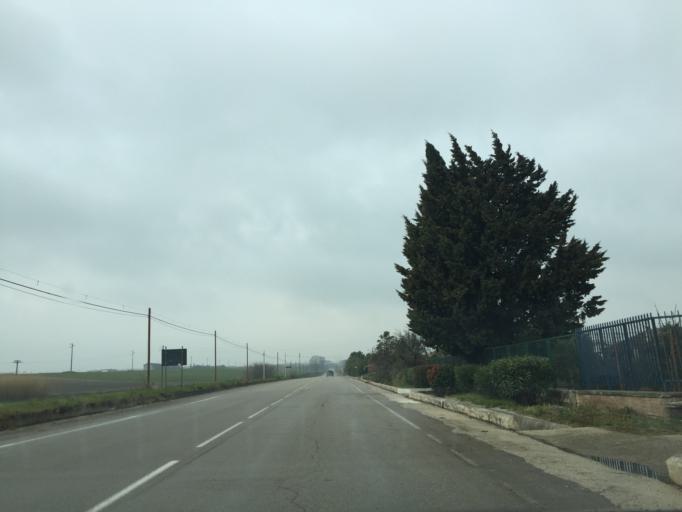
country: IT
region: Apulia
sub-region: Provincia di Foggia
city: Troia
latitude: 41.3763
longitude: 15.3588
